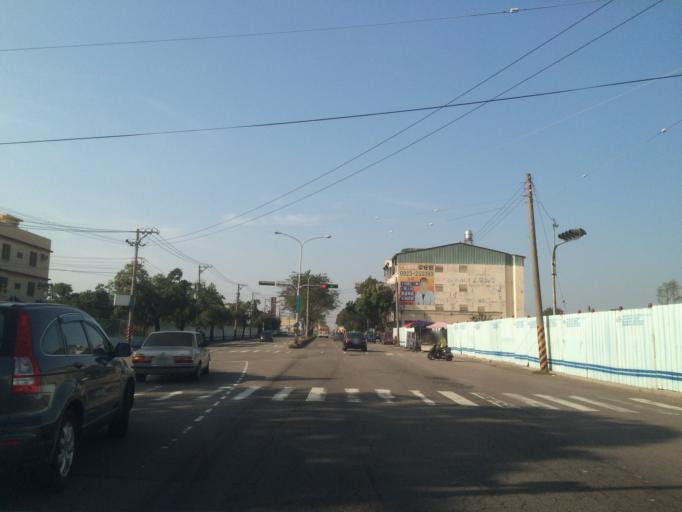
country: TW
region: Taiwan
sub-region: Taichung City
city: Taichung
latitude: 24.1840
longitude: 120.6787
